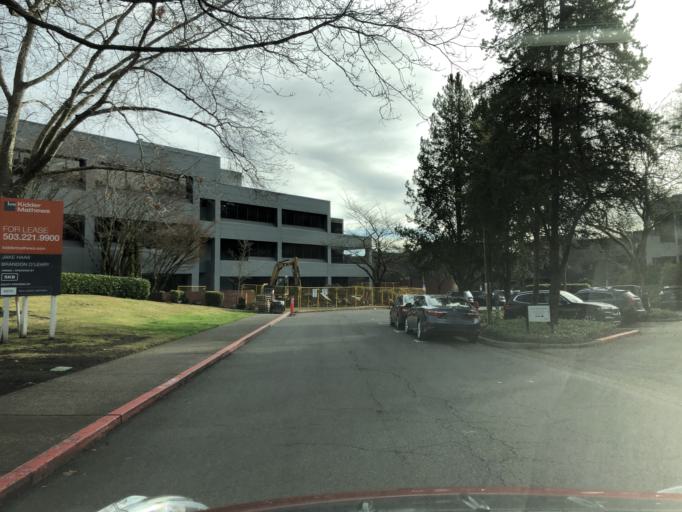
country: US
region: Oregon
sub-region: Multnomah County
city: Portland
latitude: 45.4843
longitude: -122.6739
